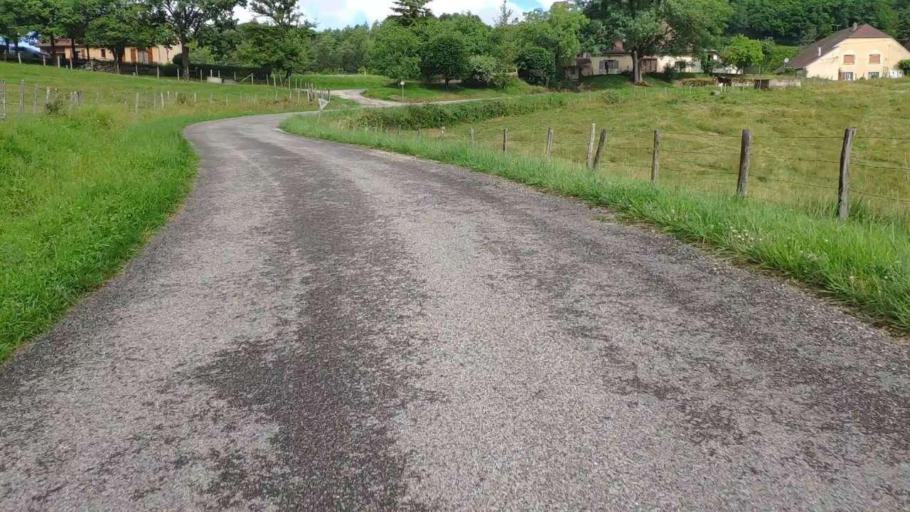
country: FR
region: Franche-Comte
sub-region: Departement du Jura
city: Poligny
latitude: 46.8241
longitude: 5.5907
